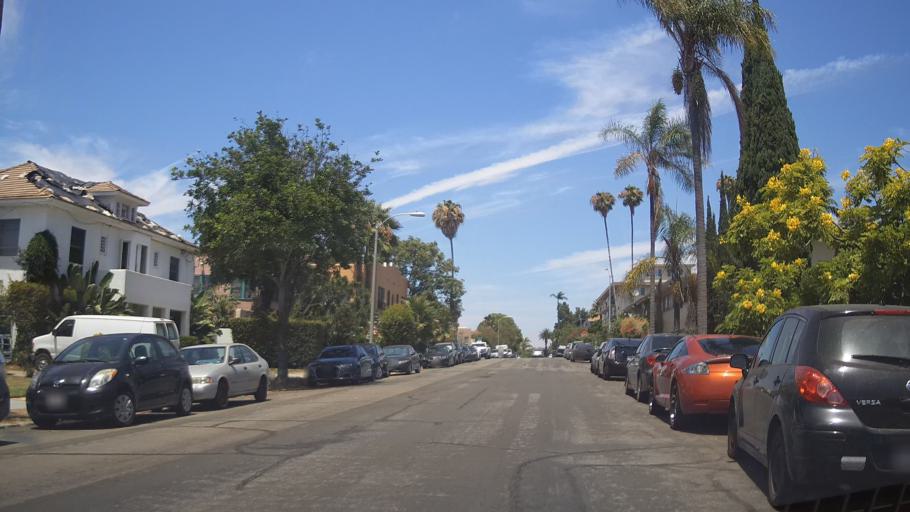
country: US
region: California
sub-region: San Diego County
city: San Diego
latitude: 32.7160
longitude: -117.1424
